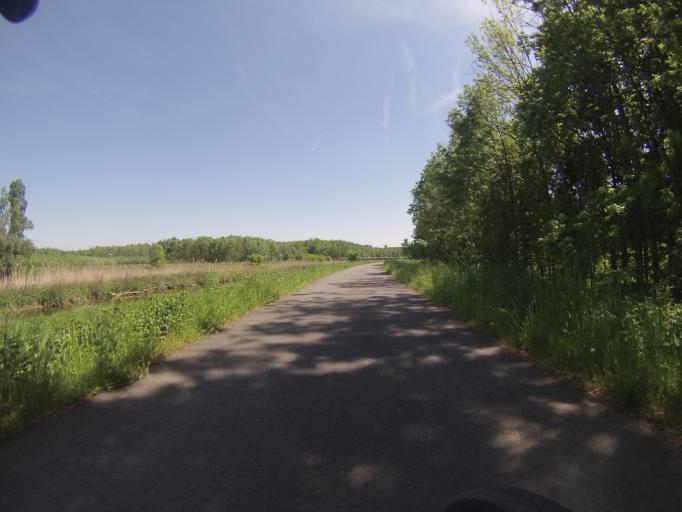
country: CZ
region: South Moravian
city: Vranovice
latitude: 48.9190
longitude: 16.5963
